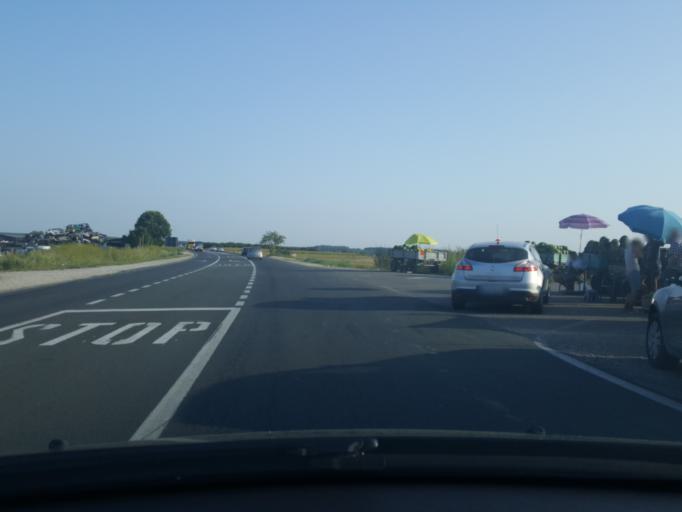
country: RS
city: Klenak
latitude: 44.7856
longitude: 19.7230
